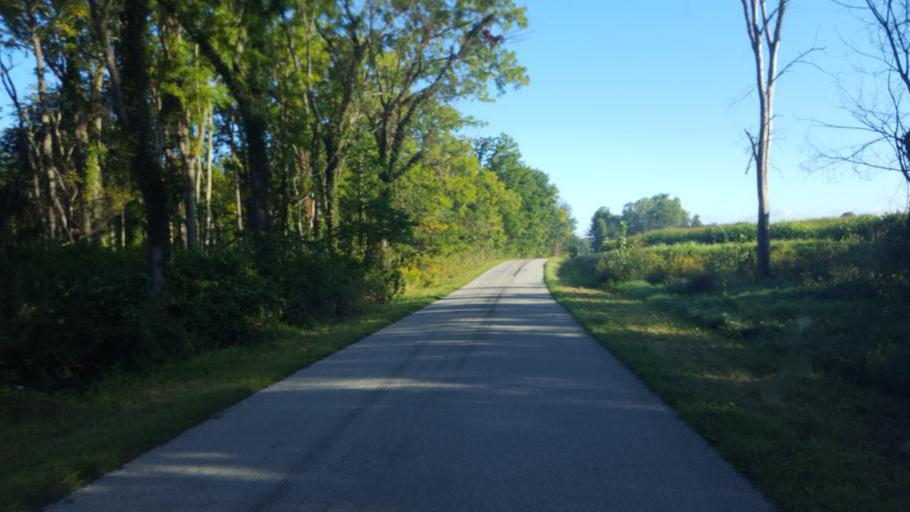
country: US
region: Ohio
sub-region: Lorain County
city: Wellington
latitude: 41.1048
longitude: -82.2788
